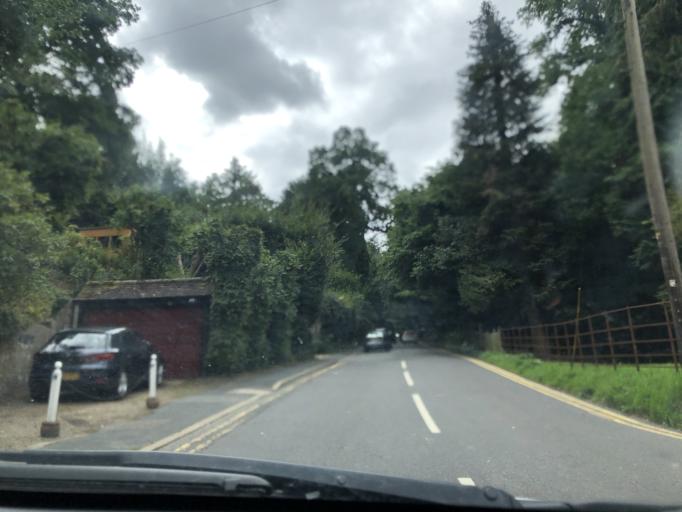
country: GB
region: England
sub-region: Kent
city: Westerham
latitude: 51.2650
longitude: 0.0782
